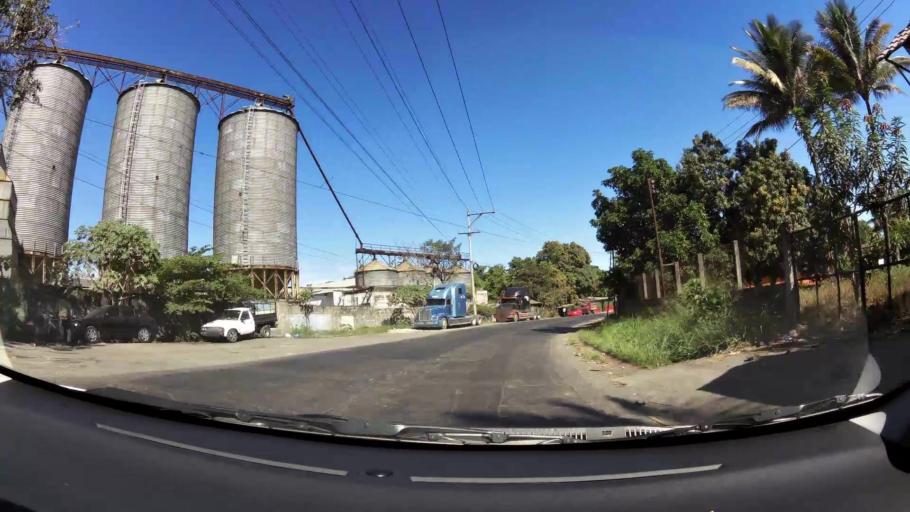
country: SV
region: La Libertad
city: Ciudad Arce
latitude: 13.7816
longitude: -89.3729
